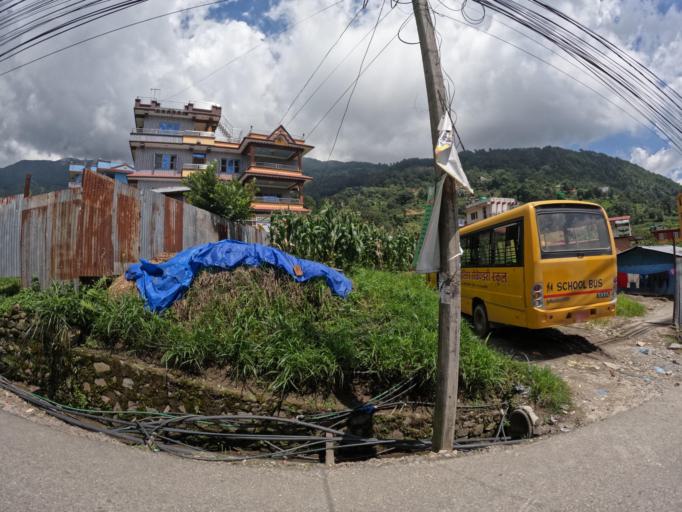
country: NP
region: Central Region
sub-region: Bagmati Zone
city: Kathmandu
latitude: 27.7930
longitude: 85.3300
